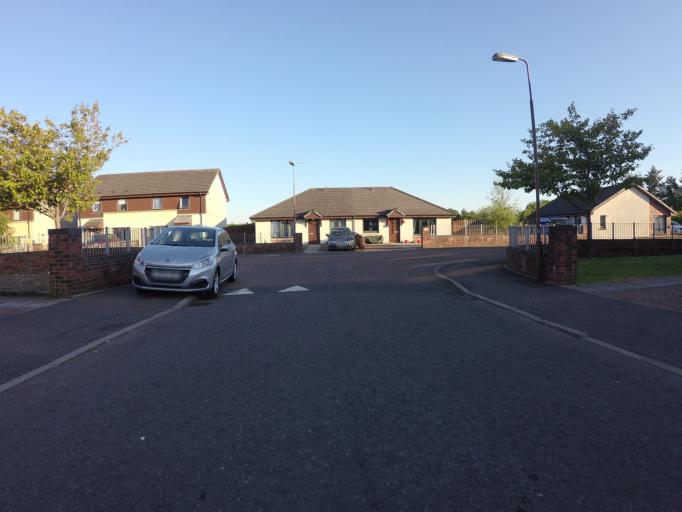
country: GB
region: Scotland
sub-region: West Lothian
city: Livingston
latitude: 55.8973
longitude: -3.5656
